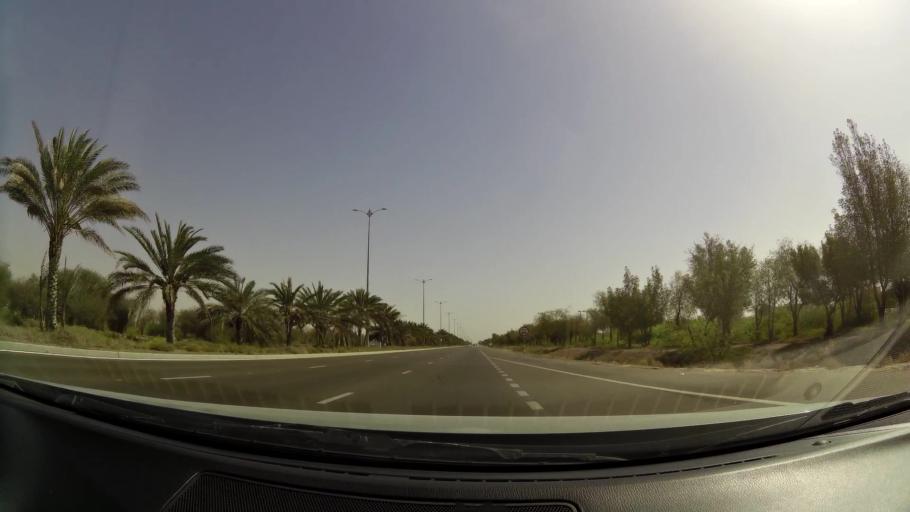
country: OM
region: Al Buraimi
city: Al Buraymi
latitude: 24.3079
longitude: 55.7942
